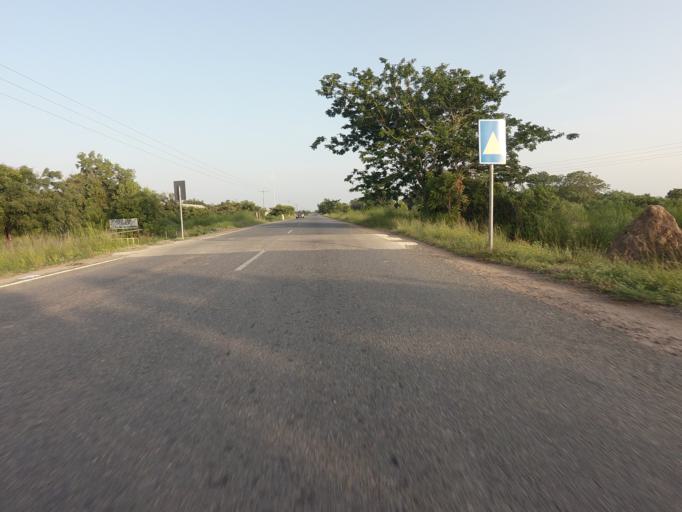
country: GH
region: Volta
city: Anloga
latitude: 5.9096
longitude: 0.7098
